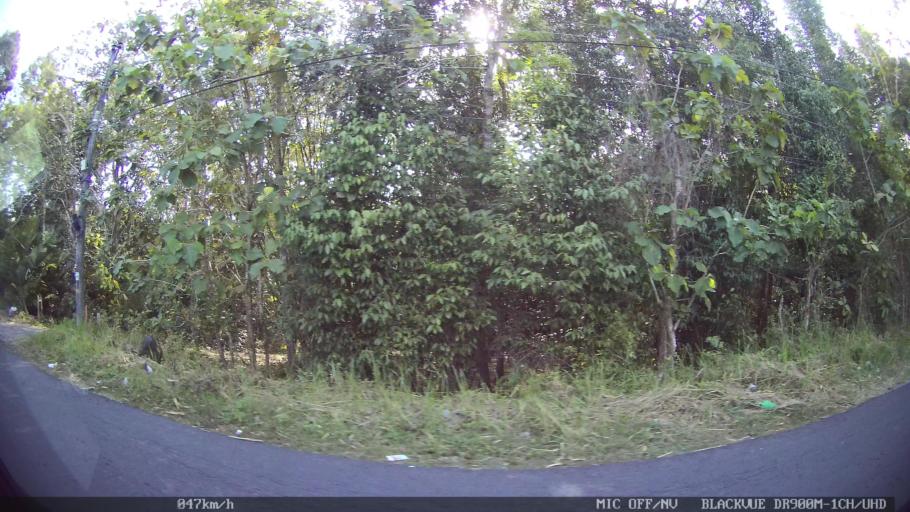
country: ID
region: Daerah Istimewa Yogyakarta
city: Bantul
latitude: -7.8625
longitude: 110.3190
